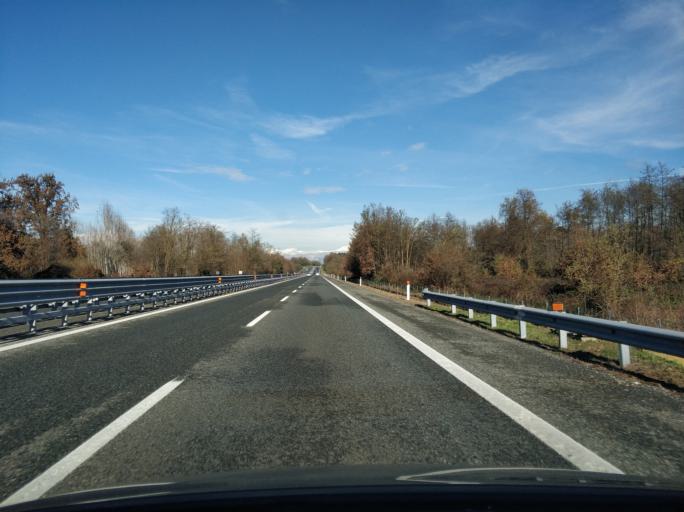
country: IT
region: Piedmont
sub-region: Provincia di Torino
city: Foglizzo
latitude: 45.2926
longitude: 7.8156
